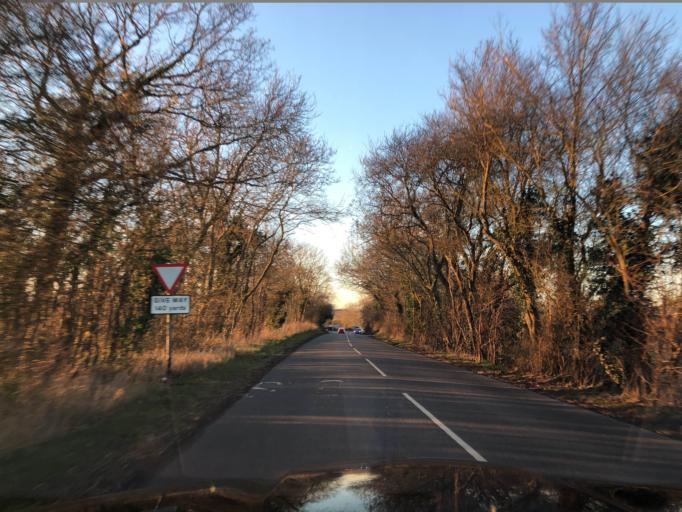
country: GB
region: England
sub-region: Warwickshire
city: Harbury
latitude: 52.2389
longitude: -1.4954
